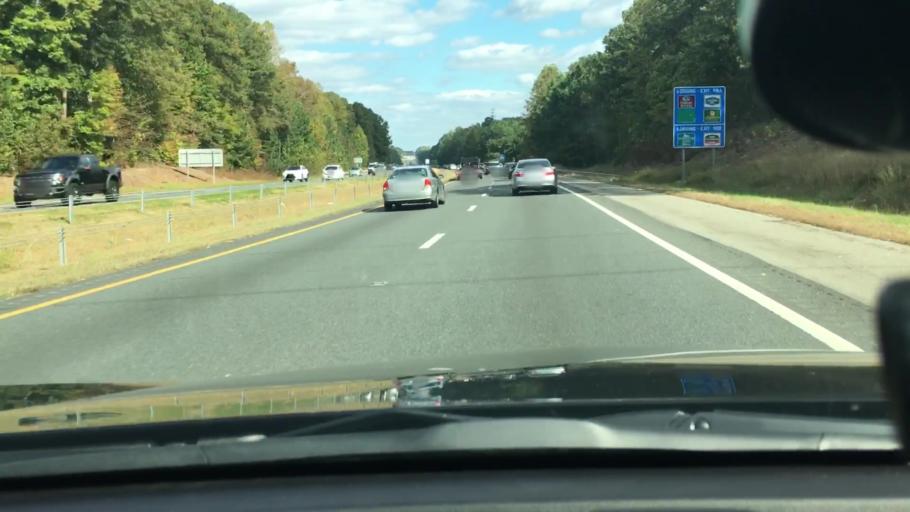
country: US
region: North Carolina
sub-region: Wake County
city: Apex
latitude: 35.7264
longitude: -78.8132
